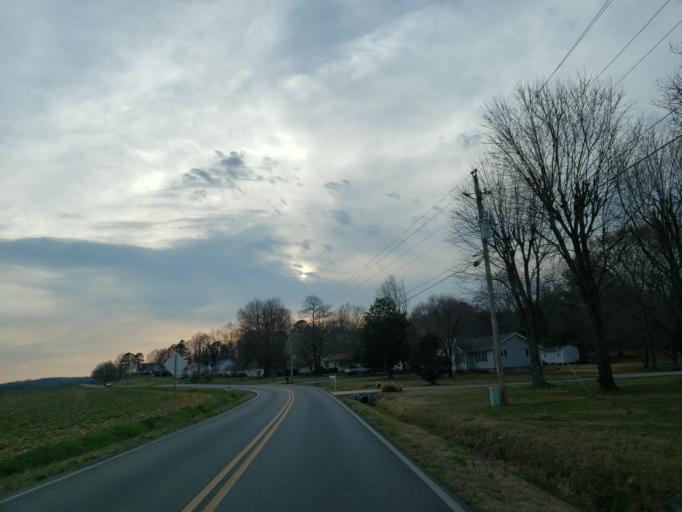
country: US
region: Georgia
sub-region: Whitfield County
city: Varnell
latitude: 34.9043
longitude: -84.9477
